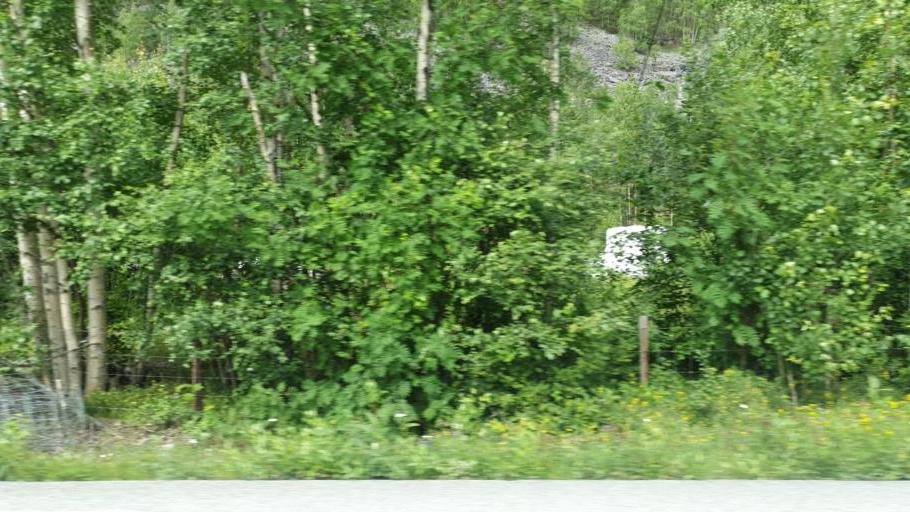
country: NO
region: Oppland
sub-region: Sel
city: Otta
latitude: 61.8439
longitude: 9.3726
